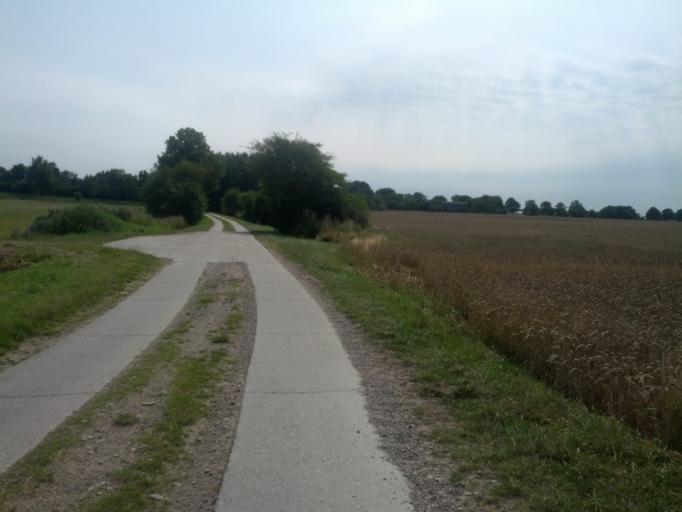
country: DE
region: Mecklenburg-Vorpommern
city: Bastorf
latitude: 54.1107
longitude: 11.6625
